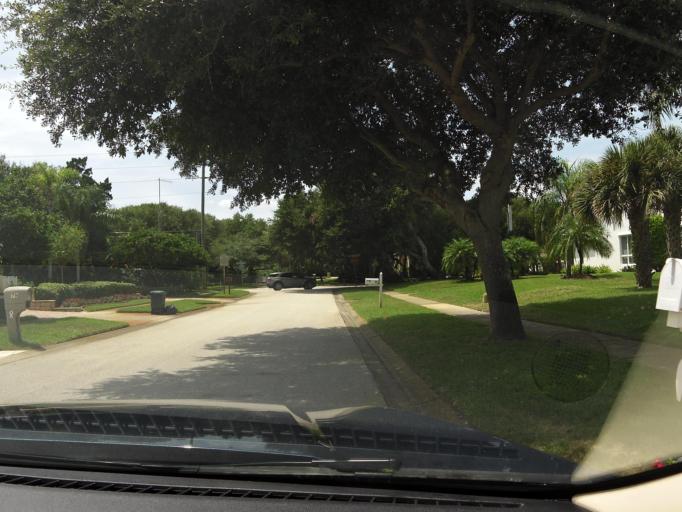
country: US
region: Florida
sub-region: Volusia County
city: Ponce Inlet
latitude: 29.0817
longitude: -80.9292
